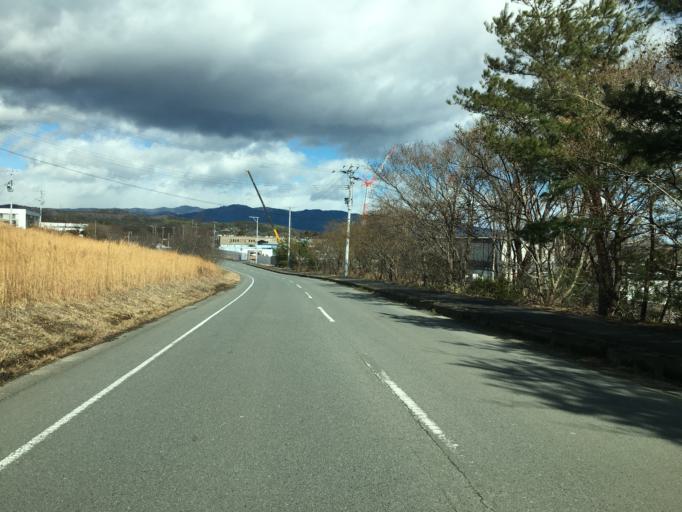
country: JP
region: Fukushima
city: Iwaki
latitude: 37.0776
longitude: 140.8410
